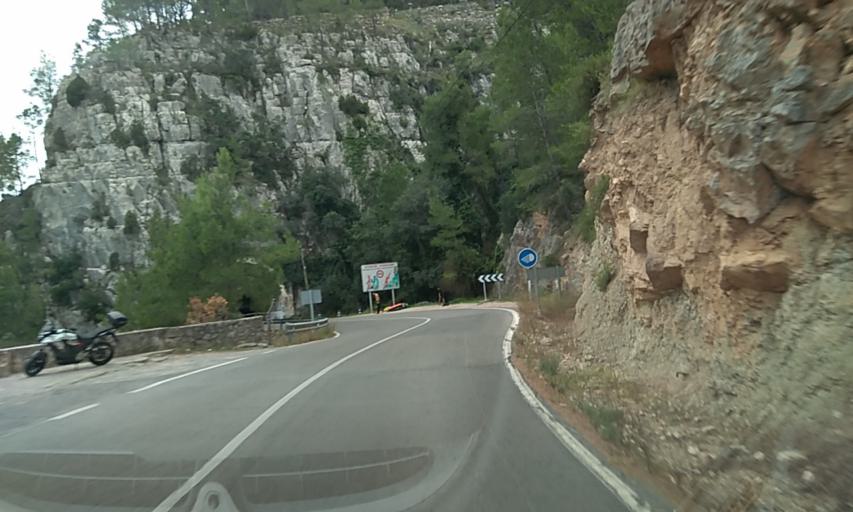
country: ES
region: Valencia
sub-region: Provincia de Castello
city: Montanejos
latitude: 40.0822
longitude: -0.5403
